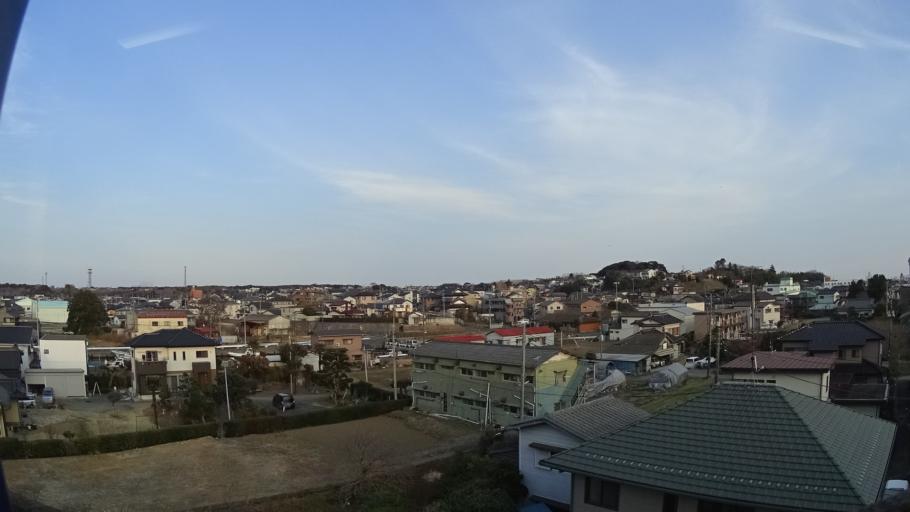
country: JP
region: Ibaraki
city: Oarai
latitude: 36.3204
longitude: 140.5647
